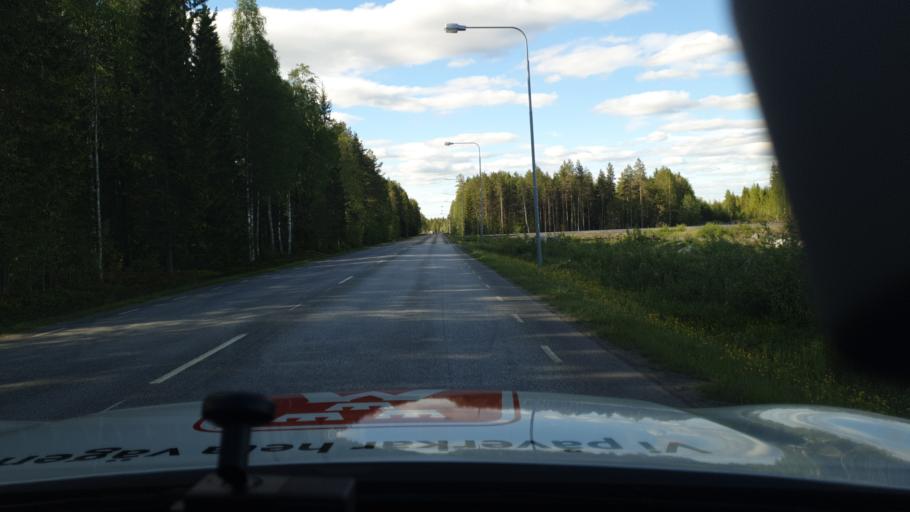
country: SE
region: Vaesterbotten
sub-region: Umea Kommun
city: Ersmark
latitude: 63.8541
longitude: 20.3442
